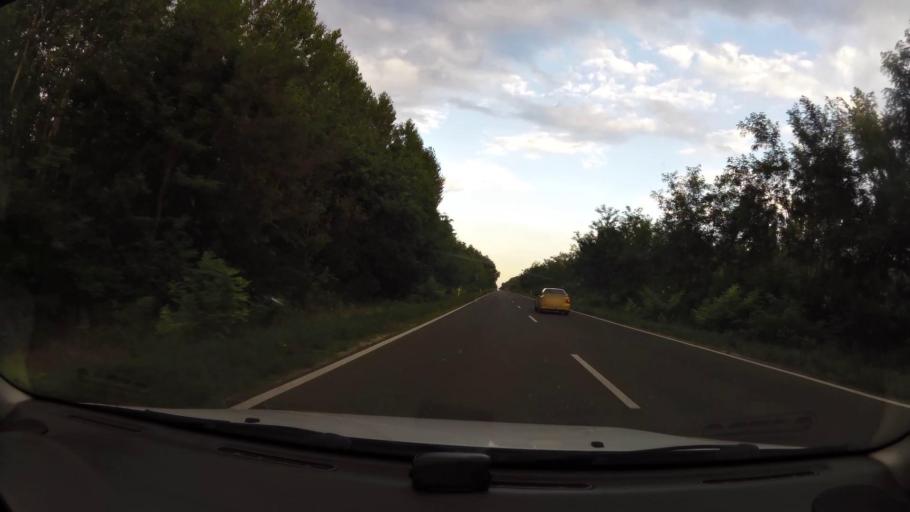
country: HU
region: Pest
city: Ujszilvas
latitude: 47.2984
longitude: 19.8934
